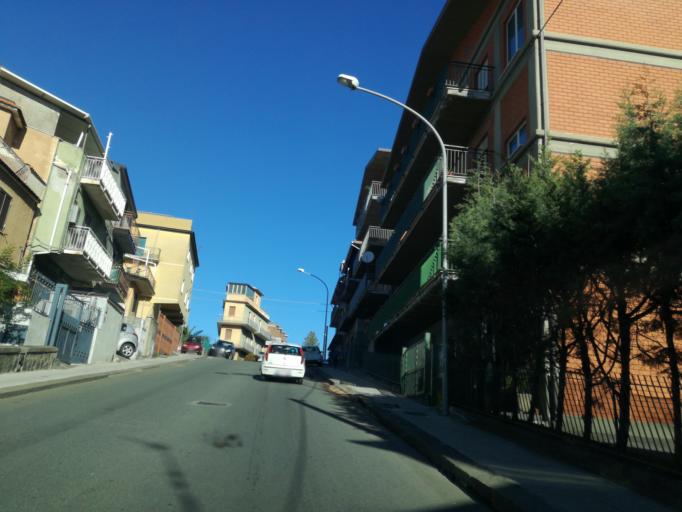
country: IT
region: Sicily
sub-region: Catania
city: Bronte
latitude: 37.7861
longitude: 14.8379
